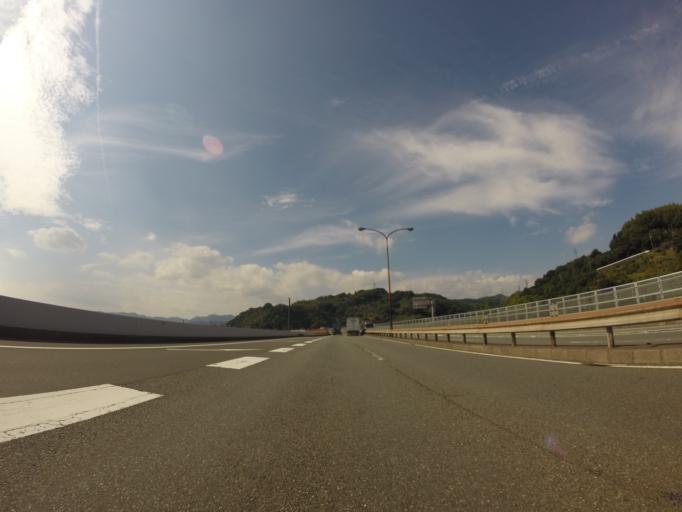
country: JP
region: Shizuoka
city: Shizuoka-shi
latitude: 35.0452
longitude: 138.5086
